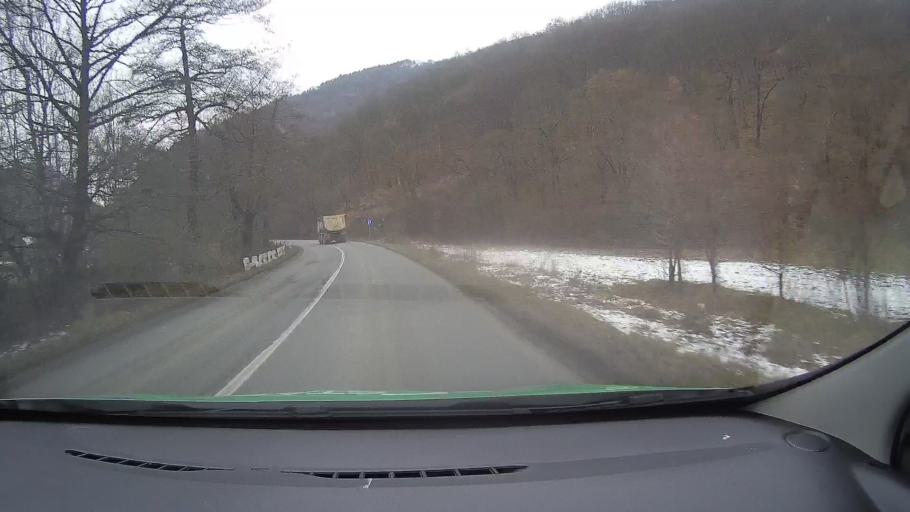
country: RO
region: Alba
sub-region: Comuna Metes
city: Metes
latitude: 46.0928
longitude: 23.3625
